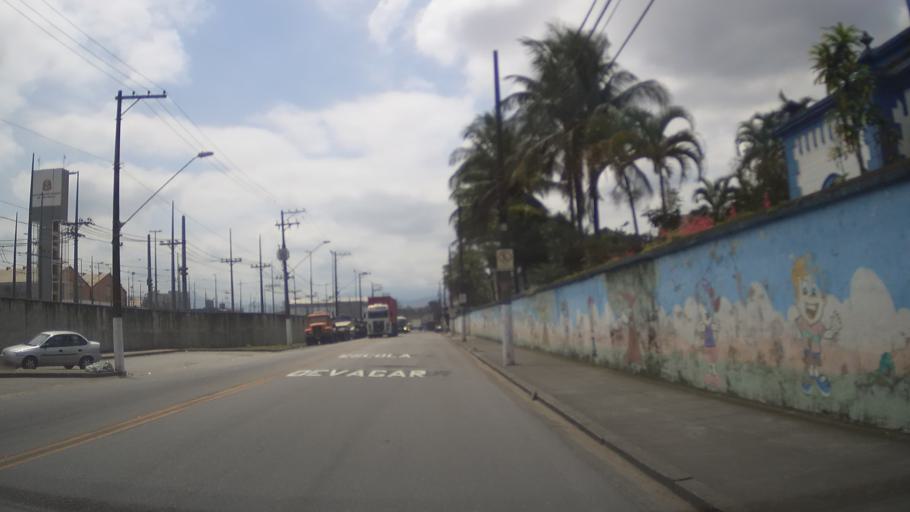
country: BR
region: Sao Paulo
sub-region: Santos
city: Santos
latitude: -23.9562
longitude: -46.3133
